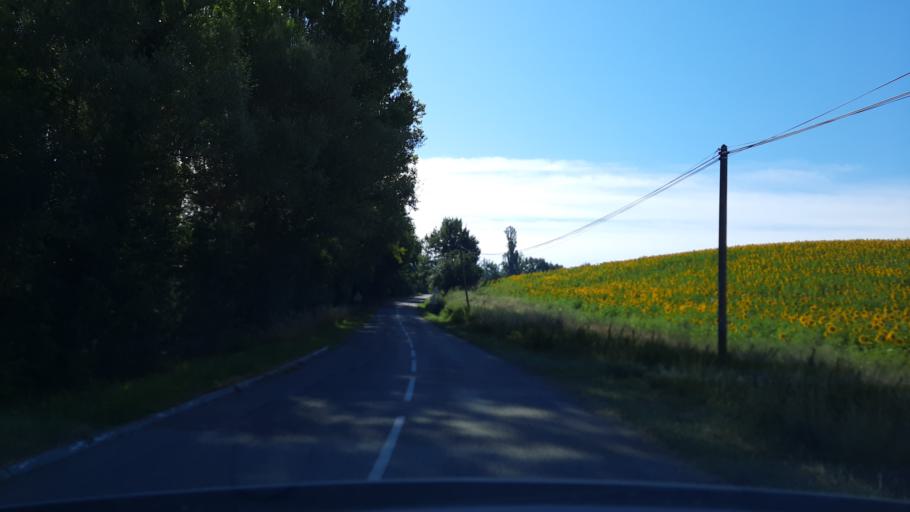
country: FR
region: Midi-Pyrenees
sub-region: Departement du Tarn-et-Garonne
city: Realville
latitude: 44.1910
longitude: 1.4548
